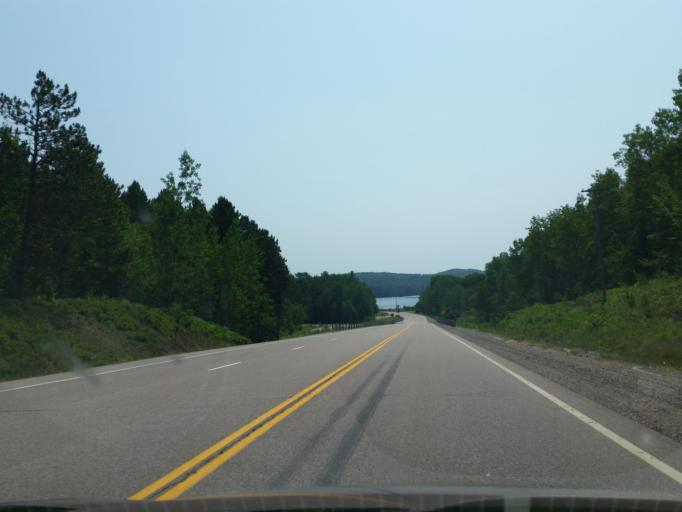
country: CA
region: Ontario
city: Deep River
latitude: 46.1718
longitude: -77.8243
